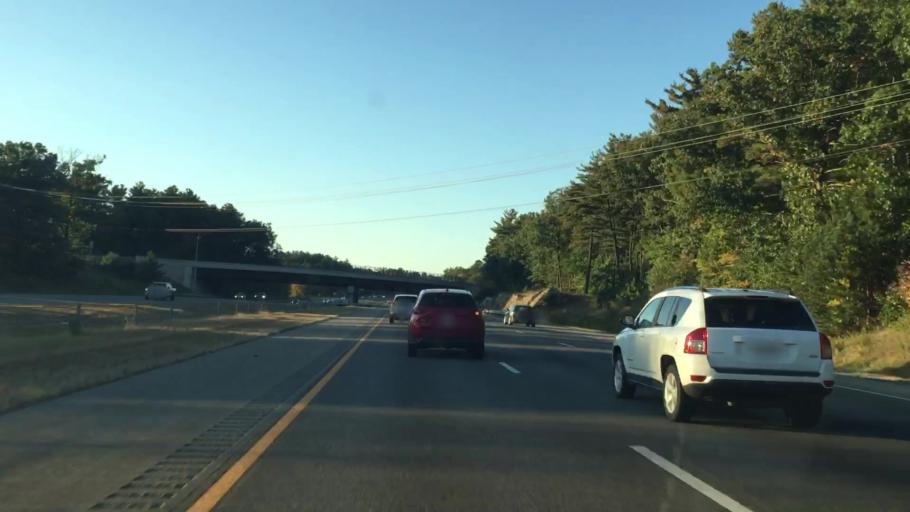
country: US
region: Massachusetts
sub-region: Middlesex County
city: Billerica
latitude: 42.5574
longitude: -71.2948
